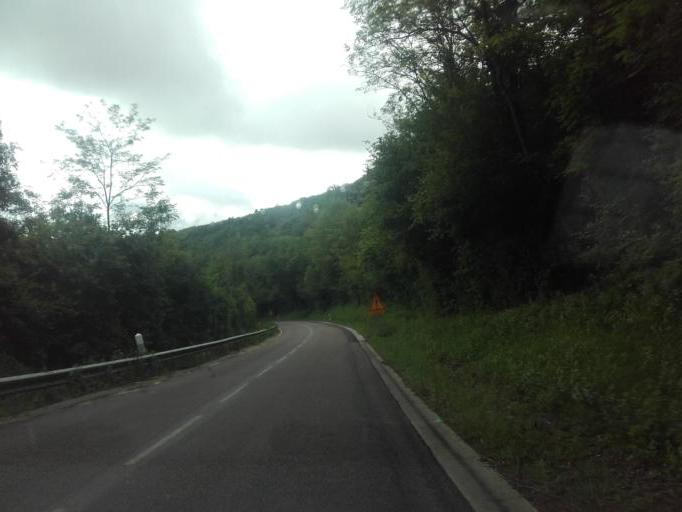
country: FR
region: Bourgogne
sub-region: Departement de la Cote-d'Or
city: Meursault
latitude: 47.0139
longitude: 4.7254
